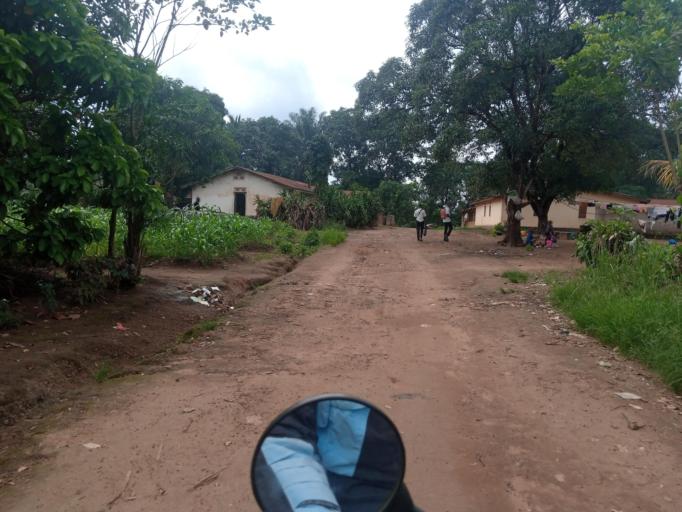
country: SL
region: Southern Province
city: Baoma
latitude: 7.9825
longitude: -11.7291
